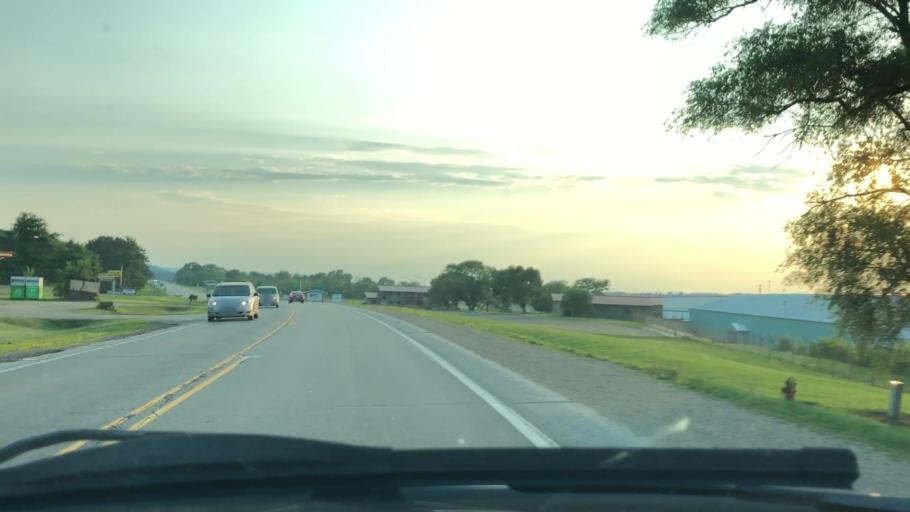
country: US
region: Wisconsin
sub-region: Dane County
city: Mazomanie
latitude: 43.1717
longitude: -89.8010
